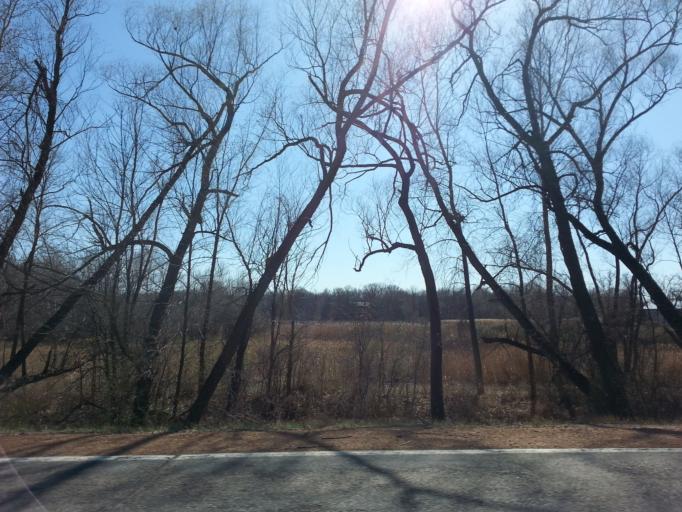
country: US
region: Minnesota
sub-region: Dakota County
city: Lakeville
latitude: 44.6539
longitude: -93.3241
